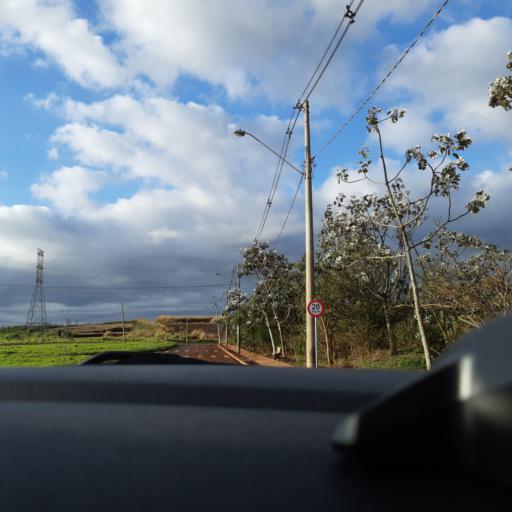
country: BR
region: Sao Paulo
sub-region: Ourinhos
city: Ourinhos
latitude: -23.0041
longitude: -49.8390
